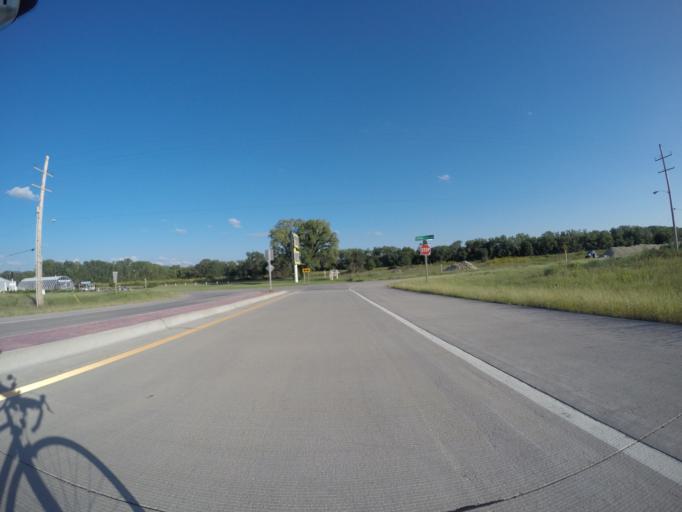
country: US
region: Kansas
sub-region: Riley County
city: Ogden
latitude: 39.1520
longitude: -96.6421
